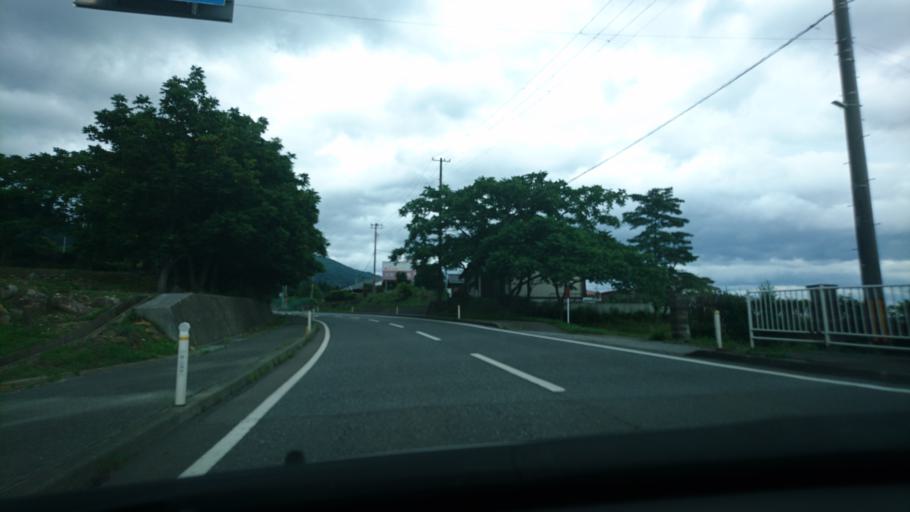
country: JP
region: Iwate
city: Kamaishi
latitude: 39.1527
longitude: 141.8357
